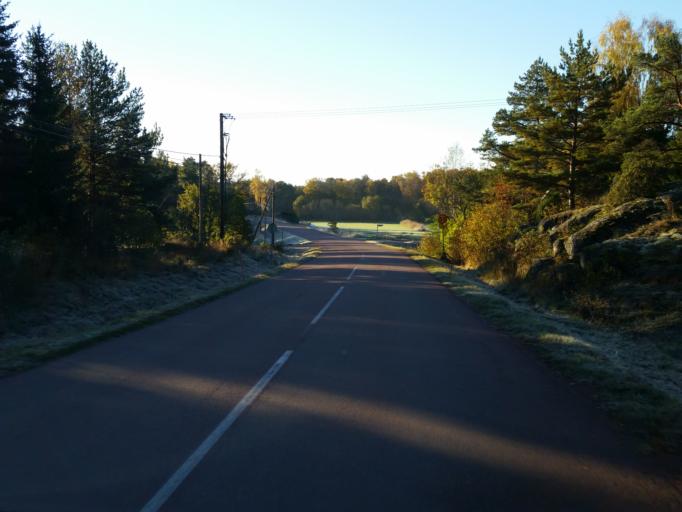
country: AX
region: Alands skaergard
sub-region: Vardoe
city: Vardoe
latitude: 60.2494
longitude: 20.3711
